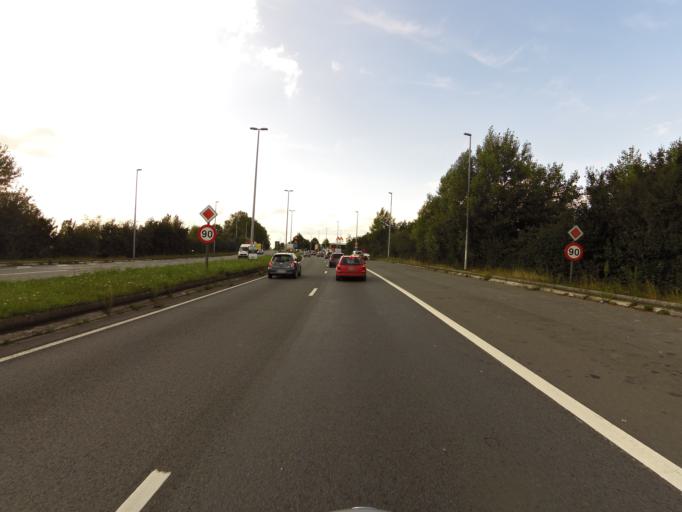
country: BE
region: Flanders
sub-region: Provincie West-Vlaanderen
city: Waregem
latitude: 50.8721
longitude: 3.4421
